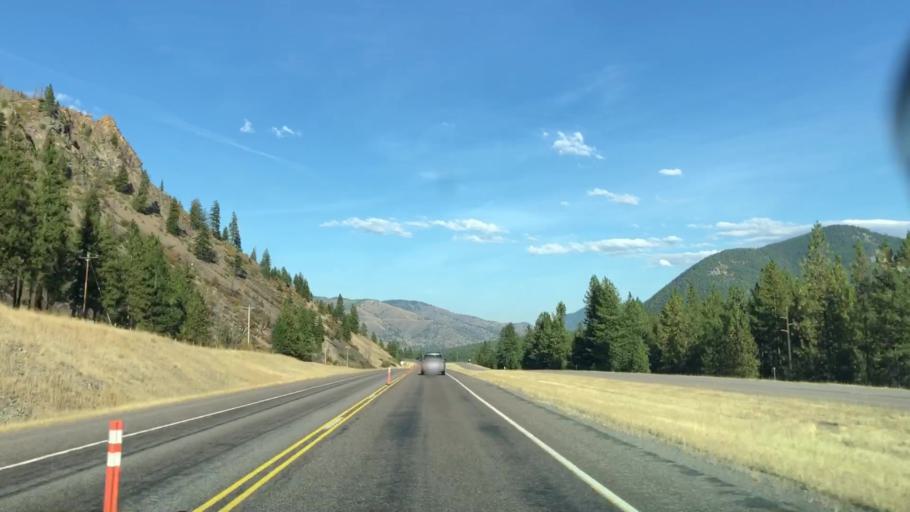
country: US
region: Montana
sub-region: Mineral County
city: Superior
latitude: 47.0124
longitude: -114.7097
